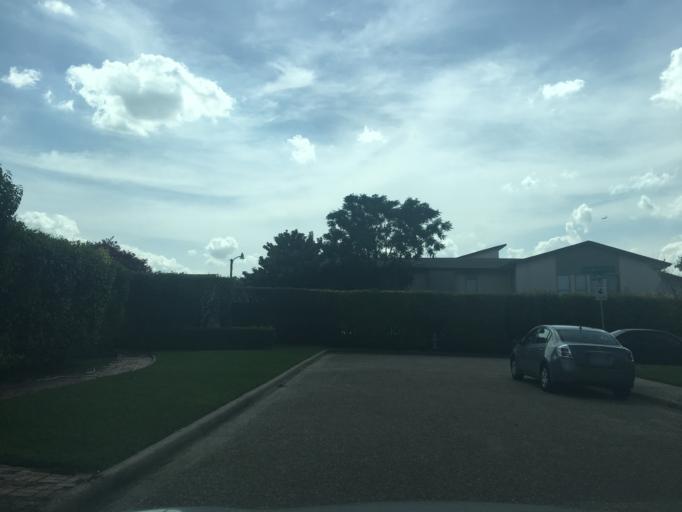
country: US
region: Texas
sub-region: Dallas County
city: Addison
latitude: 32.9228
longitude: -96.8348
